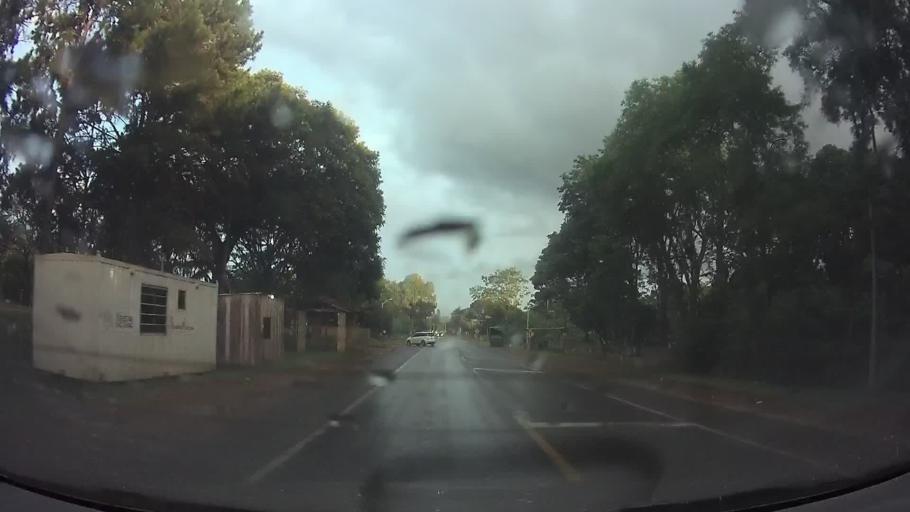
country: PY
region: Paraguari
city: Paraguari
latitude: -25.6019
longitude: -57.1928
